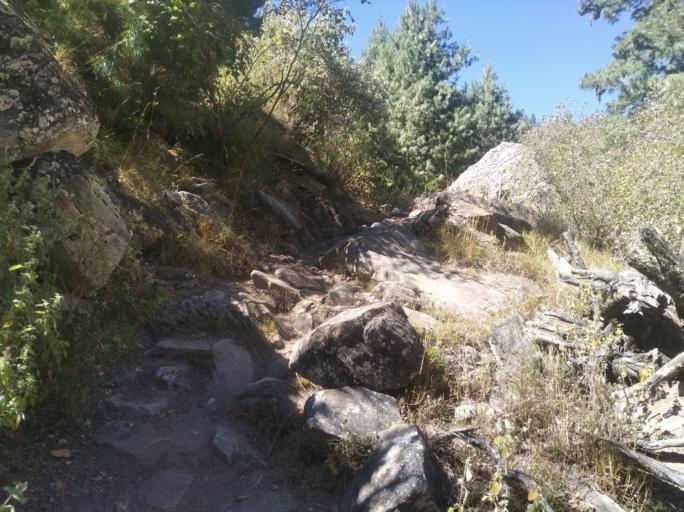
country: NP
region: Western Region
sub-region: Dhawalagiri Zone
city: Jomsom
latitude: 28.8896
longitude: 83.0730
